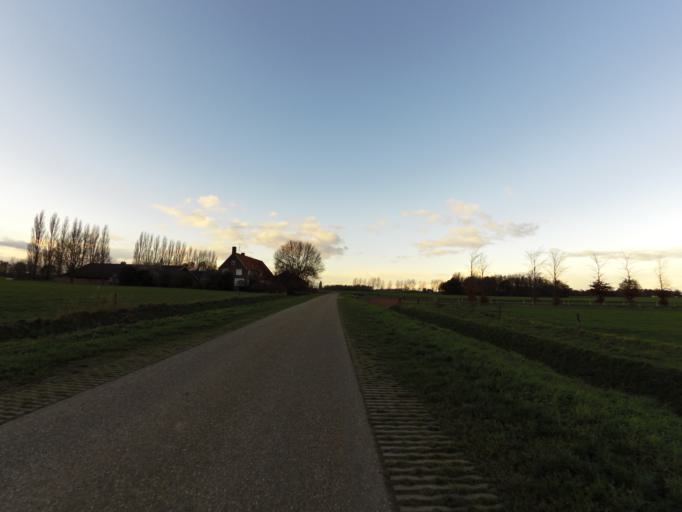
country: NL
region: Gelderland
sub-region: Oude IJsselstreek
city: Gendringen
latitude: 51.8629
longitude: 6.3512
